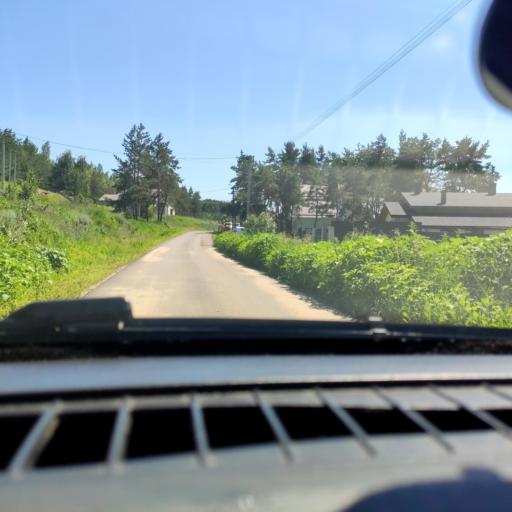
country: RU
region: Voronezj
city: Podgornoye
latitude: 51.7966
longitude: 39.1359
